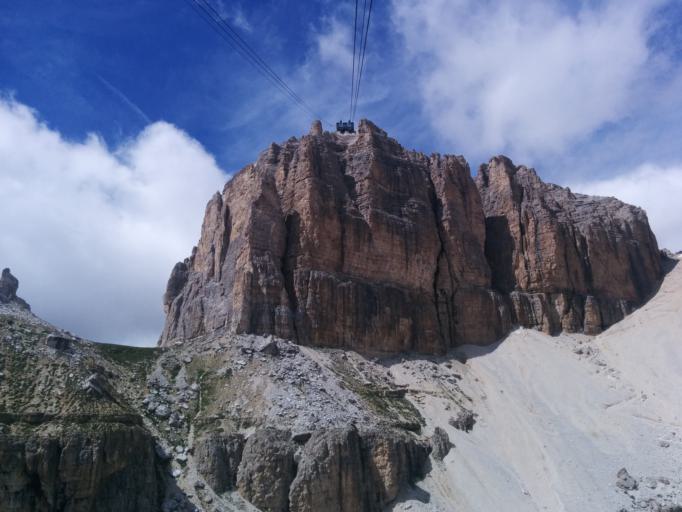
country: IT
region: Trentino-Alto Adige
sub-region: Provincia di Trento
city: Canazei
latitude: 46.4957
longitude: 11.8090
